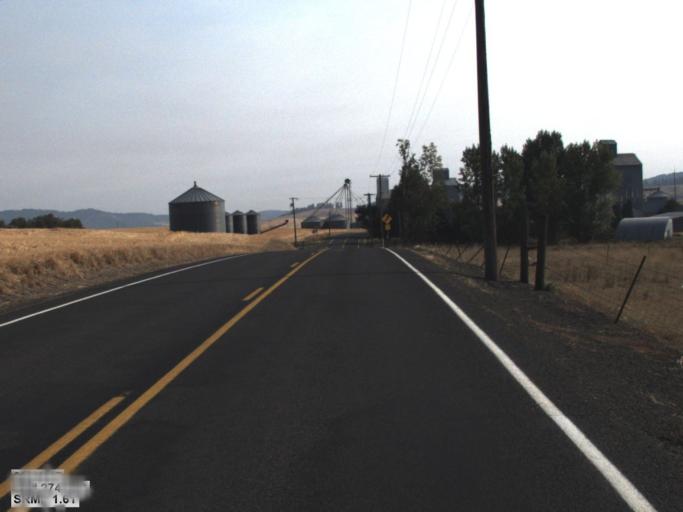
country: US
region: Idaho
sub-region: Benewah County
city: Plummer
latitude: 47.2384
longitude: -117.0456
